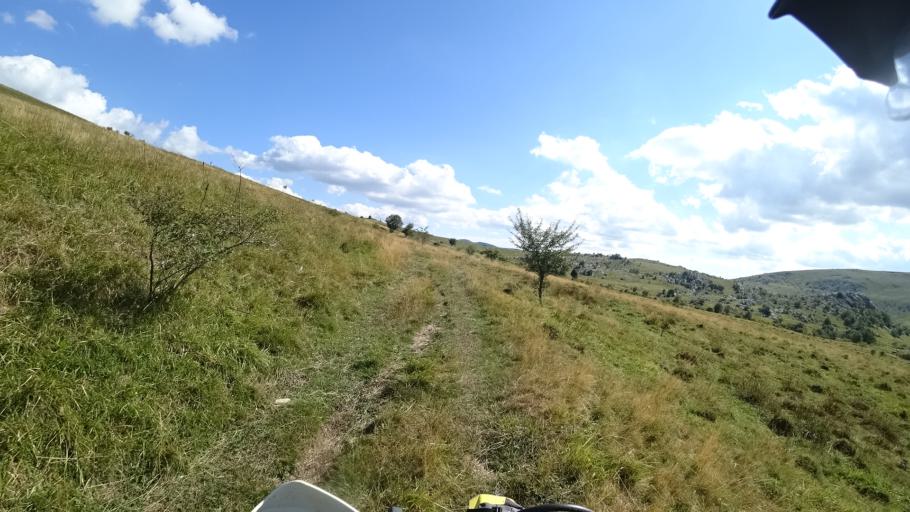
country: HR
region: Zadarska
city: Gracac
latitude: 44.3991
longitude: 16.0106
